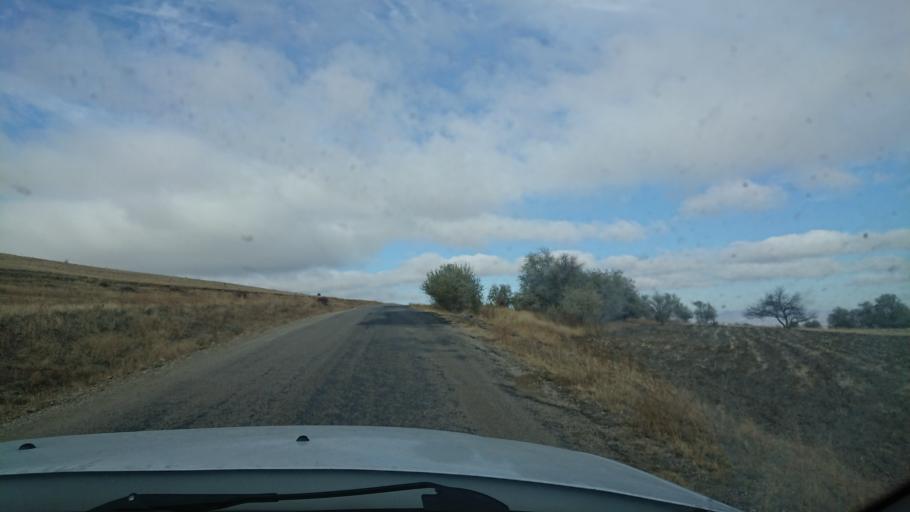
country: TR
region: Aksaray
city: Ortakoy
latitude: 38.7904
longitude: 33.9974
